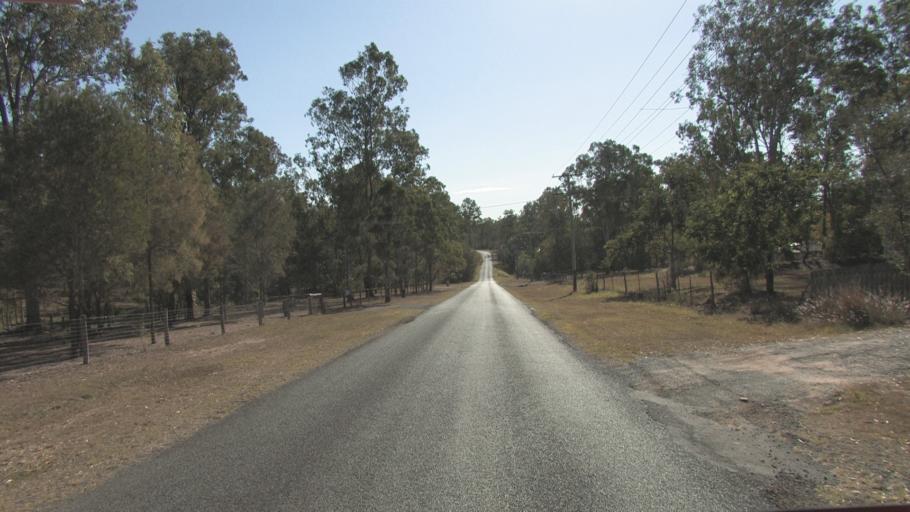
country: AU
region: Queensland
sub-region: Logan
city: Cedar Vale
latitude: -27.8267
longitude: 153.0450
